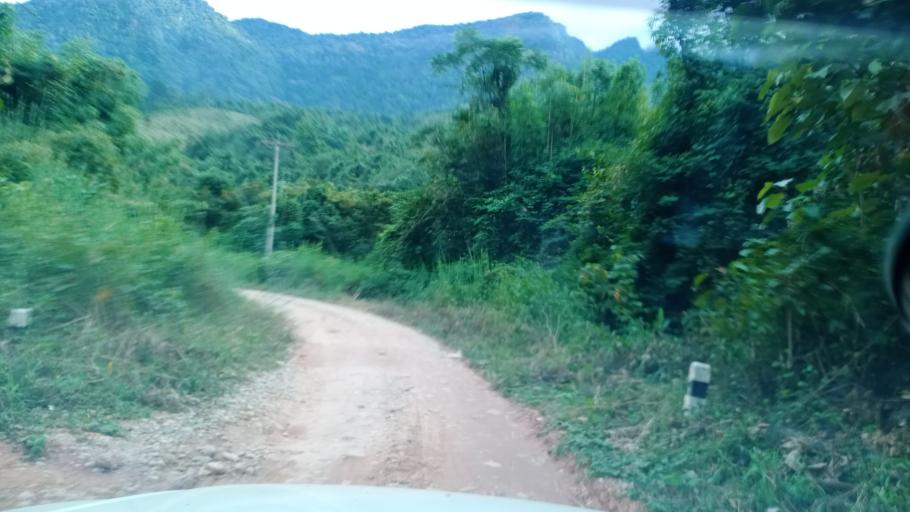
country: TH
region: Changwat Bueng Kan
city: Pak Khat
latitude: 18.7251
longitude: 103.2569
